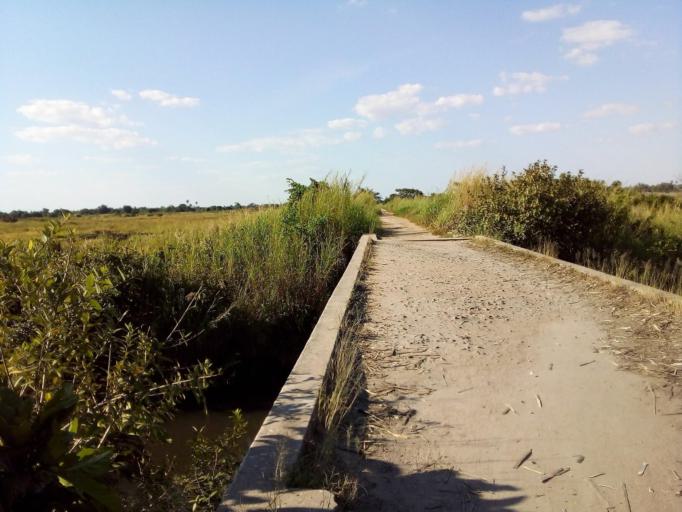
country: MZ
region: Zambezia
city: Quelimane
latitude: -17.5826
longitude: 36.8445
